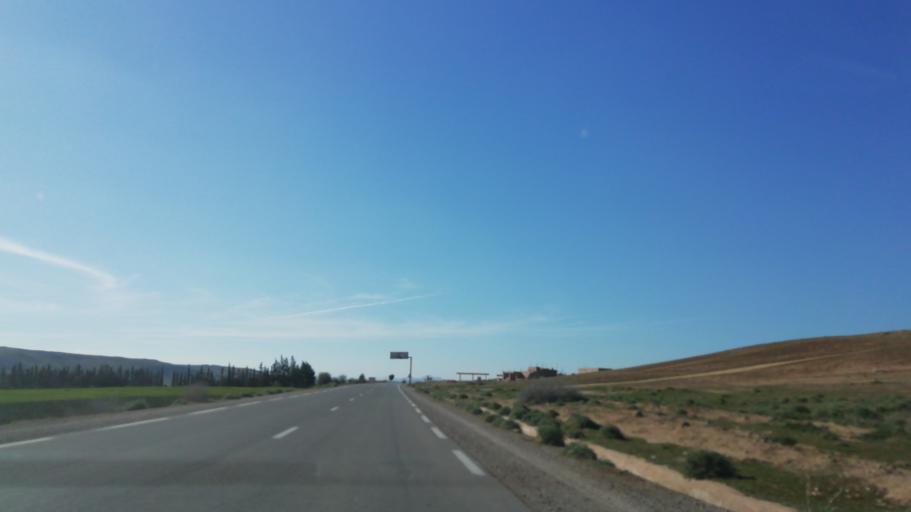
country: DZ
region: Mascara
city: Oued el Abtal
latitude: 35.4503
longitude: 0.7855
